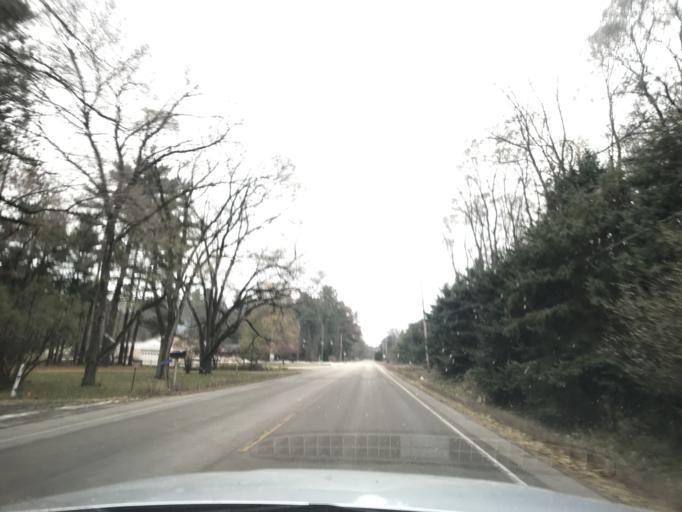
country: US
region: Wisconsin
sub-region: Marinette County
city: Marinette
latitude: 45.0678
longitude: -87.6193
